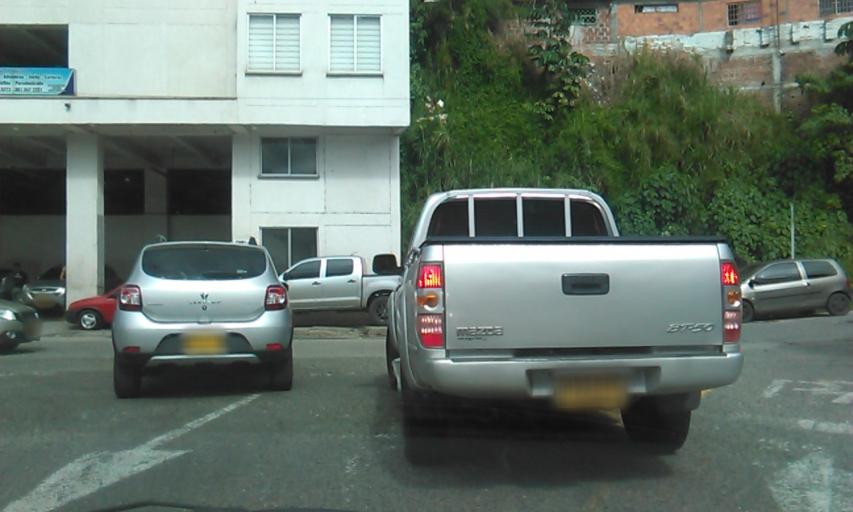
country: CO
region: Quindio
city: Armenia
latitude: 4.5331
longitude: -75.6707
